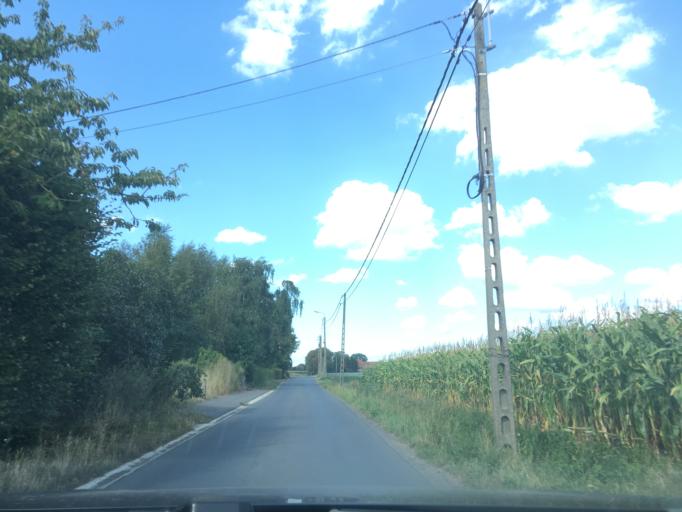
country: BE
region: Flanders
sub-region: Provincie West-Vlaanderen
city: Staden
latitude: 50.9748
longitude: 3.0408
